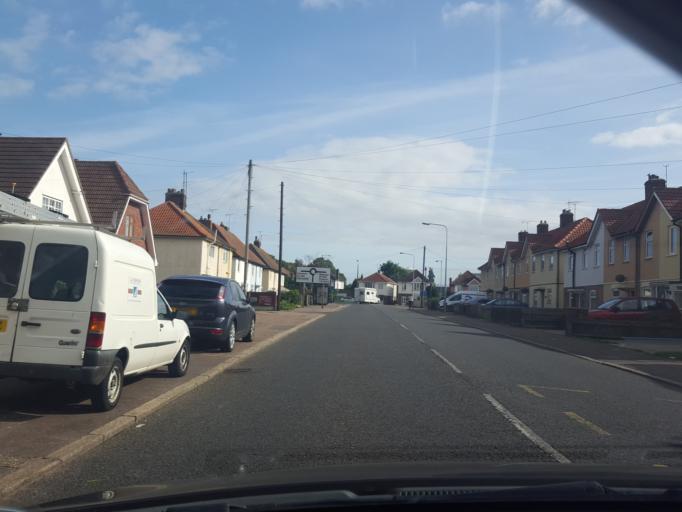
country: GB
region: England
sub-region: Essex
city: Dovercourt
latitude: 51.9356
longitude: 1.2597
